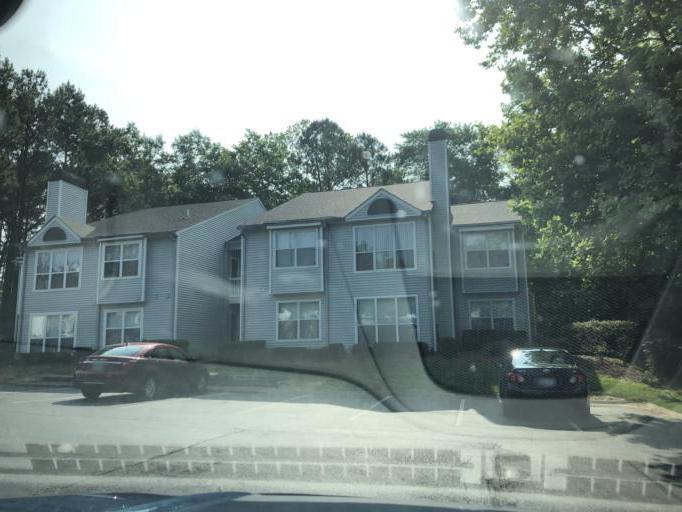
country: US
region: Tennessee
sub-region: Rutherford County
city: La Vergne
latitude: 36.0537
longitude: -86.6397
